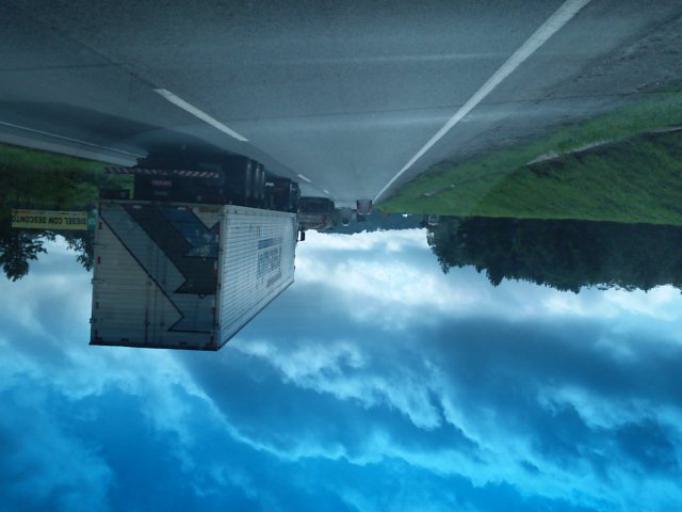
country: BR
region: Parana
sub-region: Antonina
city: Antonina
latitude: -25.1034
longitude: -48.7030
